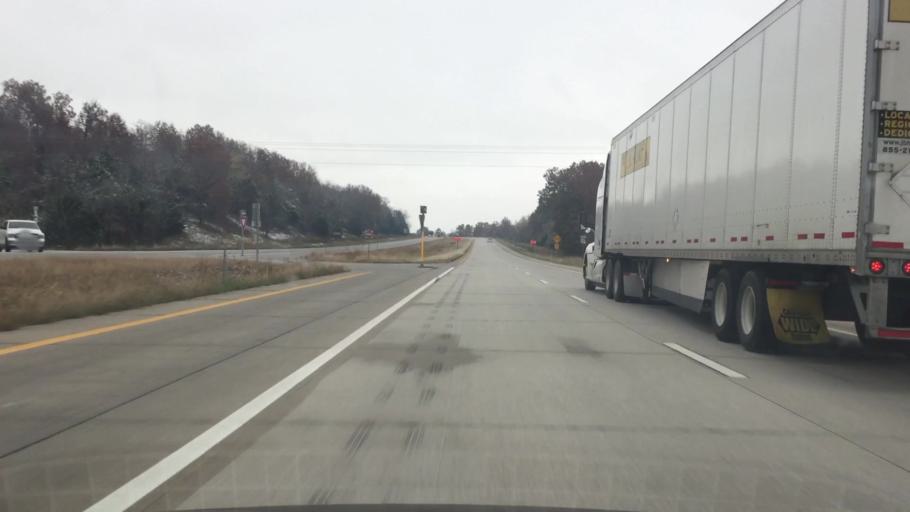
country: US
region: Missouri
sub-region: Henry County
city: Clinton
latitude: 38.2212
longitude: -93.7615
